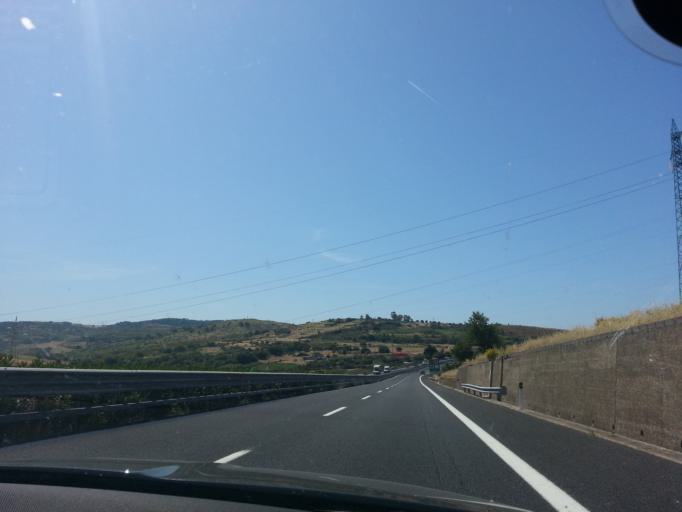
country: IT
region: Latium
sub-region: Citta metropolitana di Roma Capitale
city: Aurelia
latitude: 42.1292
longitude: 11.8223
